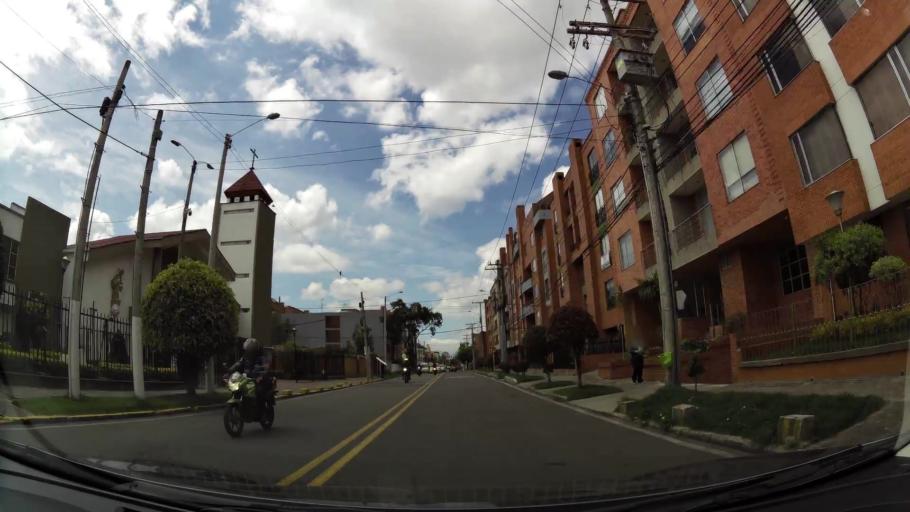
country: CO
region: Bogota D.C.
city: Barrio San Luis
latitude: 4.7051
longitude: -74.0586
